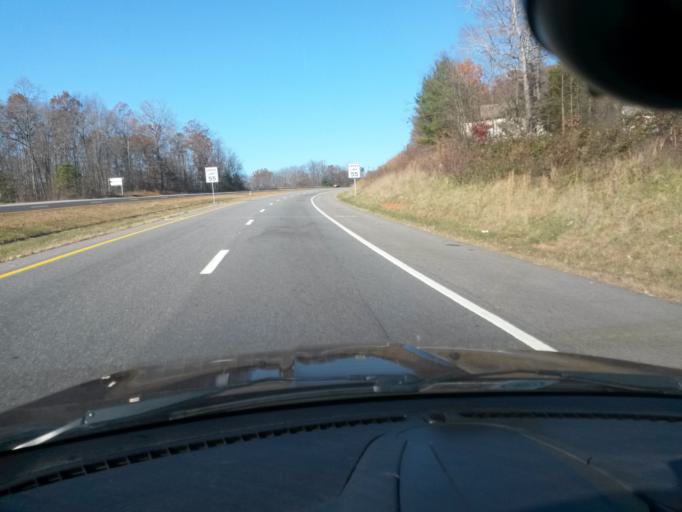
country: US
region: Virginia
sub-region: Patrick County
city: Stuart
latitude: 36.6464
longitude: -80.2647
